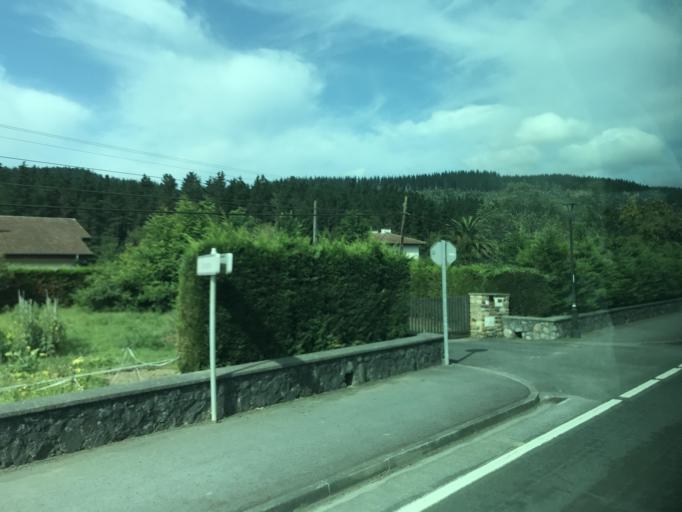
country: ES
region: Basque Country
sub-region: Bizkaia
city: Areatza
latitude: 43.1495
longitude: -2.7666
